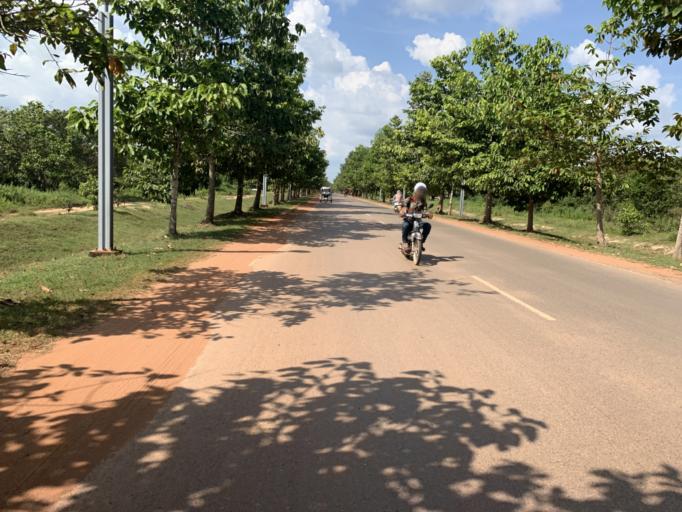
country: KH
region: Siem Reap
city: Siem Reap
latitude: 13.3843
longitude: 103.8793
